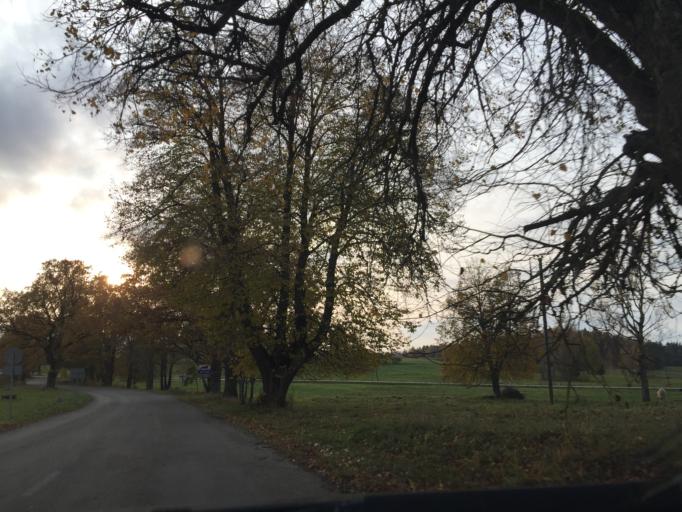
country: LV
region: Pargaujas
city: Stalbe
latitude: 57.3337
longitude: 25.1360
